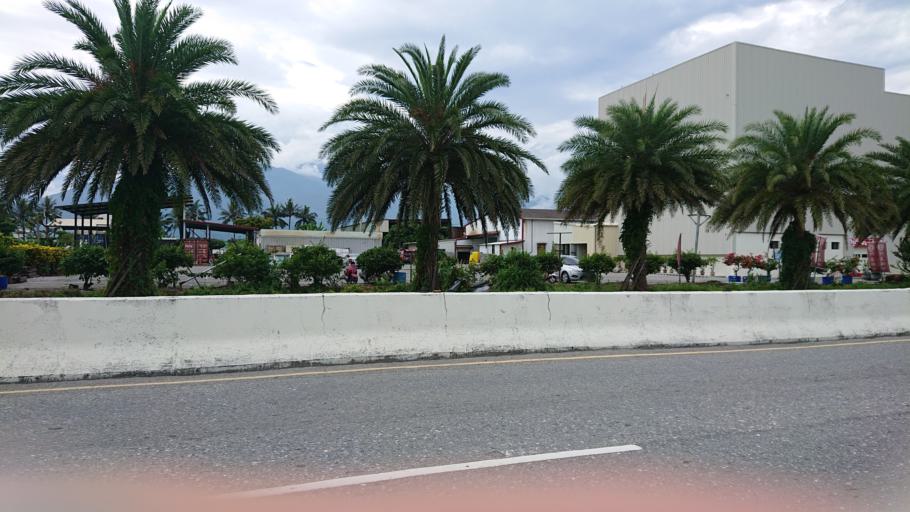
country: TW
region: Taiwan
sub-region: Hualien
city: Hualian
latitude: 23.9467
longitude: 121.5975
